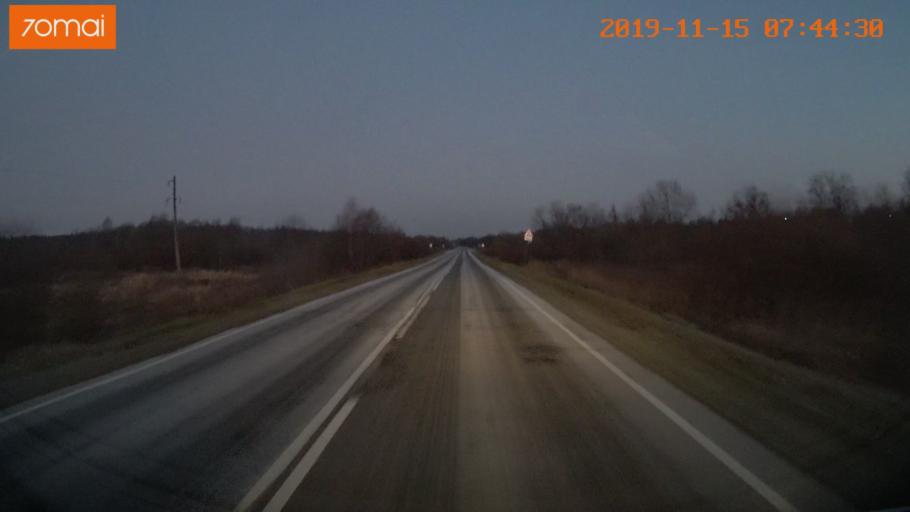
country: RU
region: Vologda
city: Sheksna
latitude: 58.8143
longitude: 38.3118
